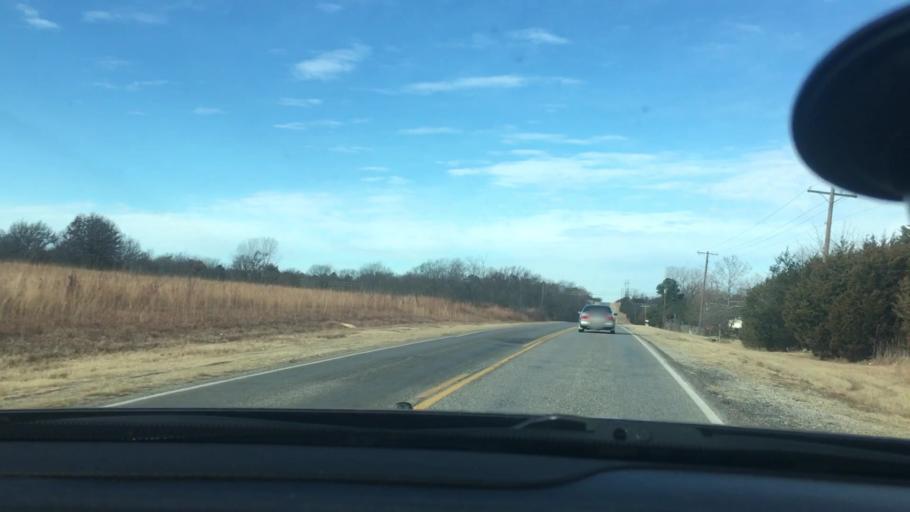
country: US
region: Oklahoma
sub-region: Seminole County
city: Konawa
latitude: 34.9457
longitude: -96.7274
